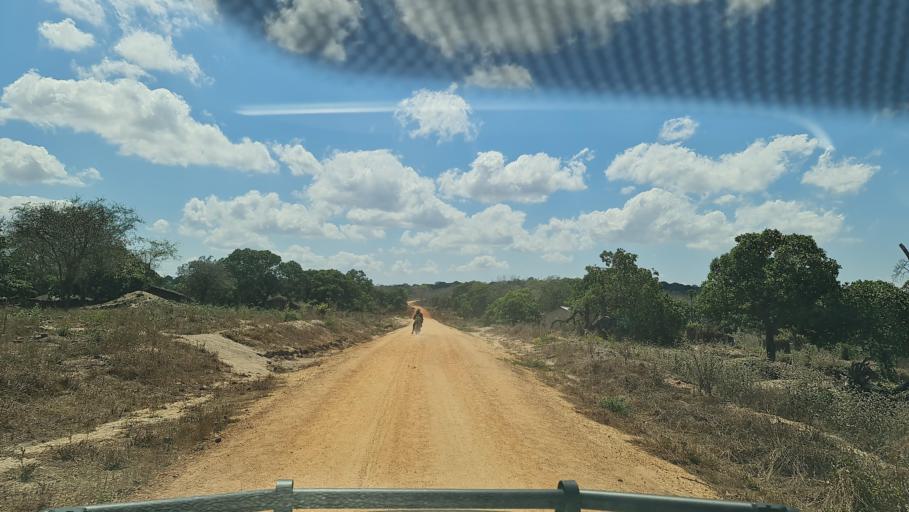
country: MZ
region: Nampula
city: Nacala
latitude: -14.1691
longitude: 40.2494
